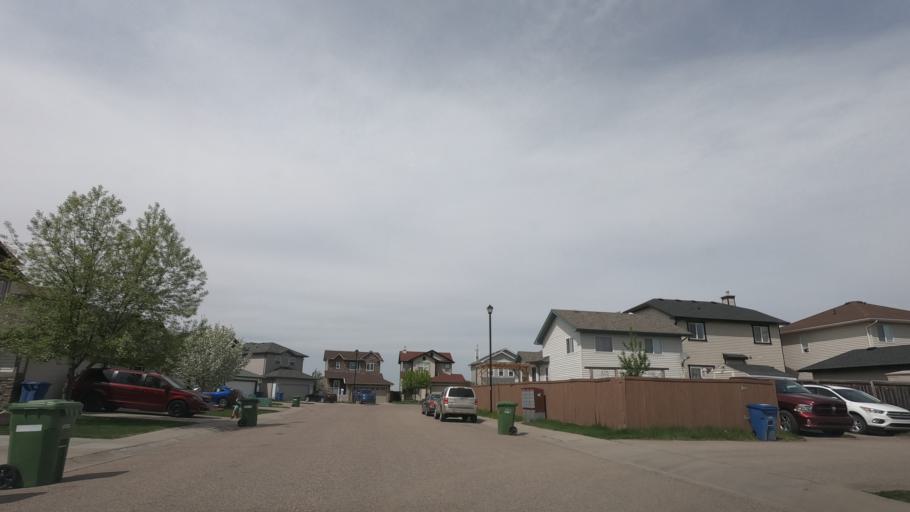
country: CA
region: Alberta
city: Airdrie
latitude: 51.3065
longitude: -114.0244
